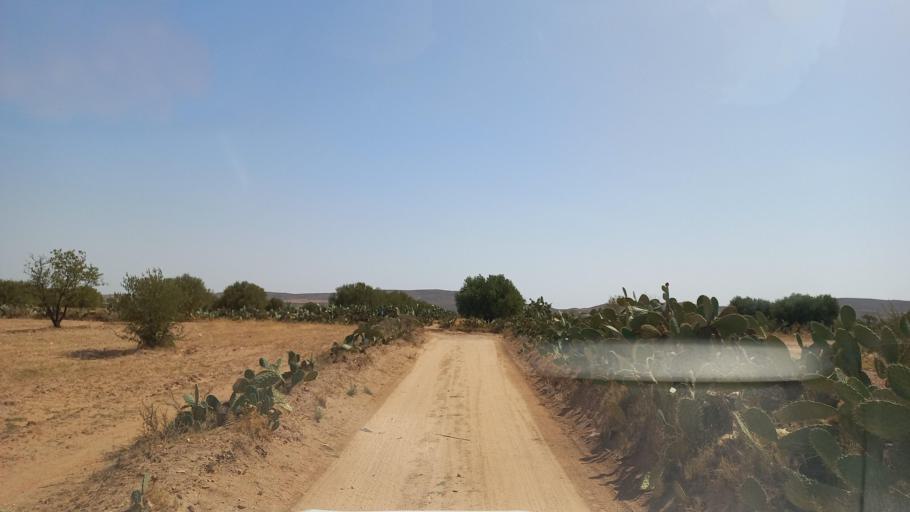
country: TN
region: Al Qasrayn
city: Kasserine
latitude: 35.2181
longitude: 9.0363
